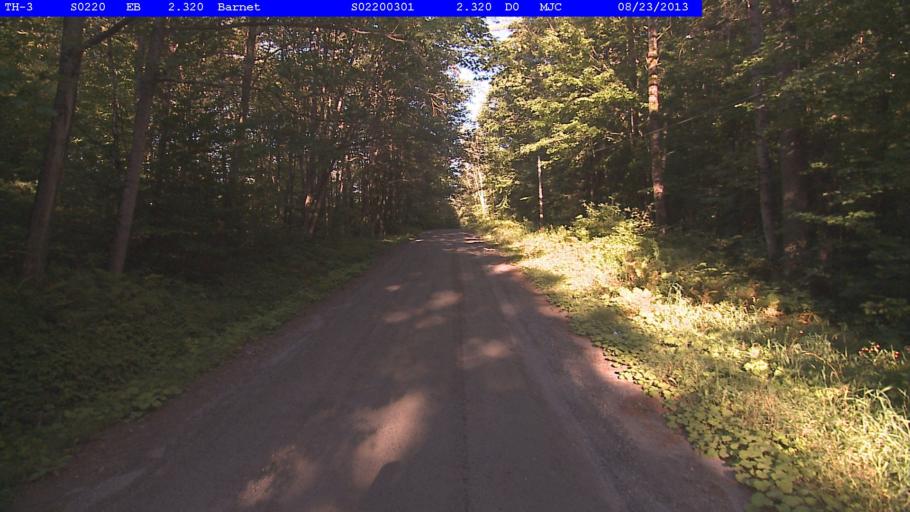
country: US
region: Vermont
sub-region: Caledonia County
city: Saint Johnsbury
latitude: 44.3311
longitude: -72.0081
